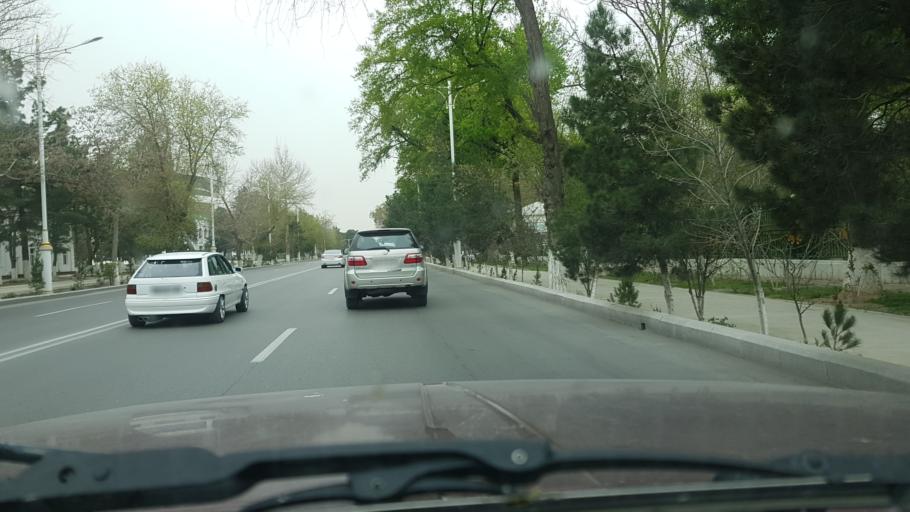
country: TM
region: Ahal
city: Ashgabat
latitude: 37.9487
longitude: 58.3480
